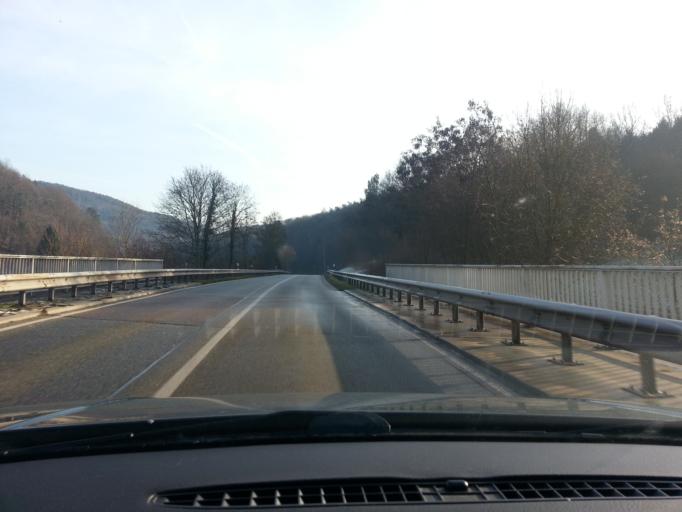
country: DE
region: Rheinland-Pfalz
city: Munchweiler am Klingbach
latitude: 49.1487
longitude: 7.9664
